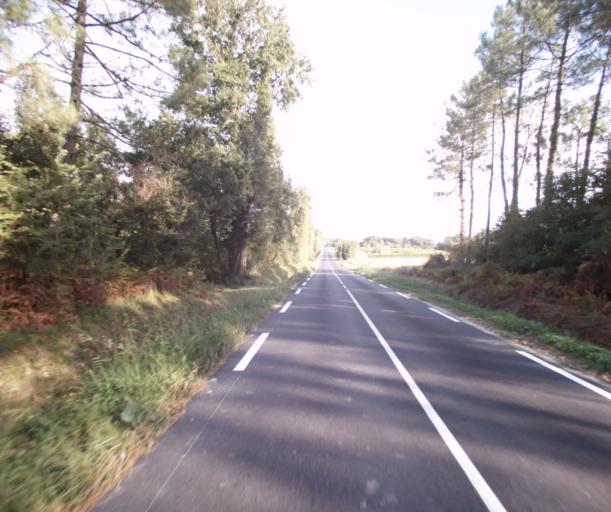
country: FR
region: Midi-Pyrenees
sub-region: Departement du Gers
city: Eauze
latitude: 43.8732
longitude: 0.0402
